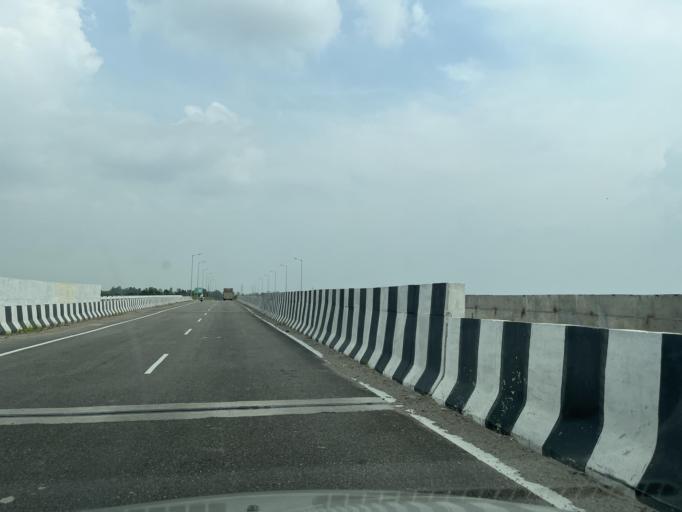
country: IN
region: Uttarakhand
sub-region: Udham Singh Nagar
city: Kashipur
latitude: 29.1736
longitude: 78.9465
